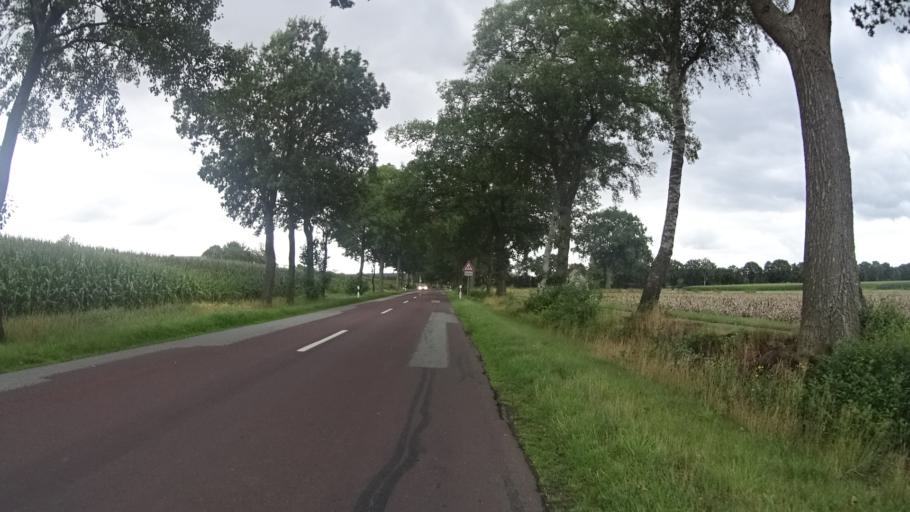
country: DE
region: Lower Saxony
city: Kuhrstedt
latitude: 53.6045
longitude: 8.8167
